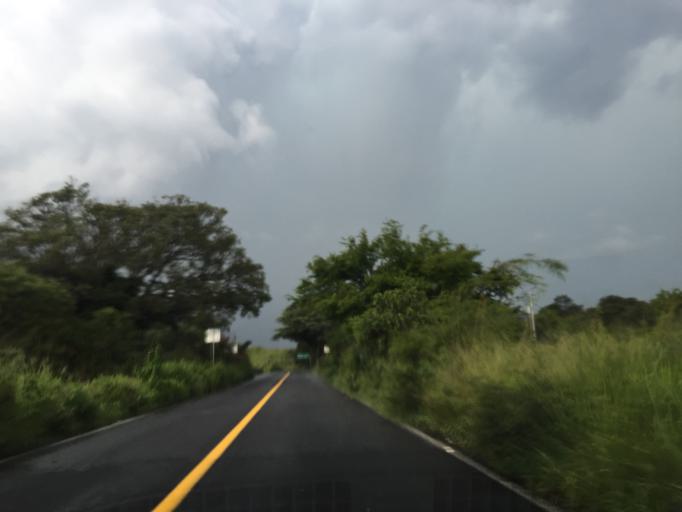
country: MX
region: Colima
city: Queseria
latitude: 19.3928
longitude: -103.5641
